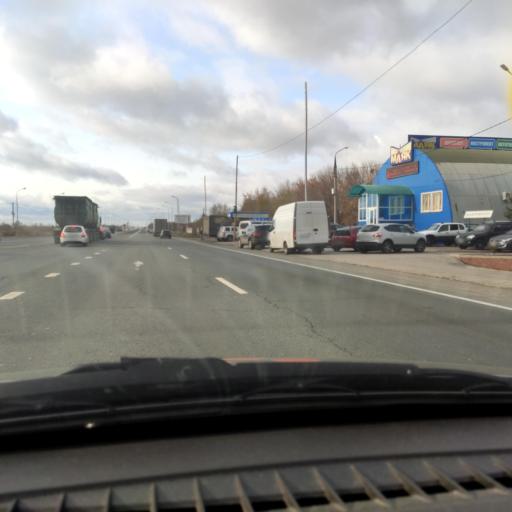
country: RU
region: Samara
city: Tol'yatti
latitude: 53.5726
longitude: 49.4612
